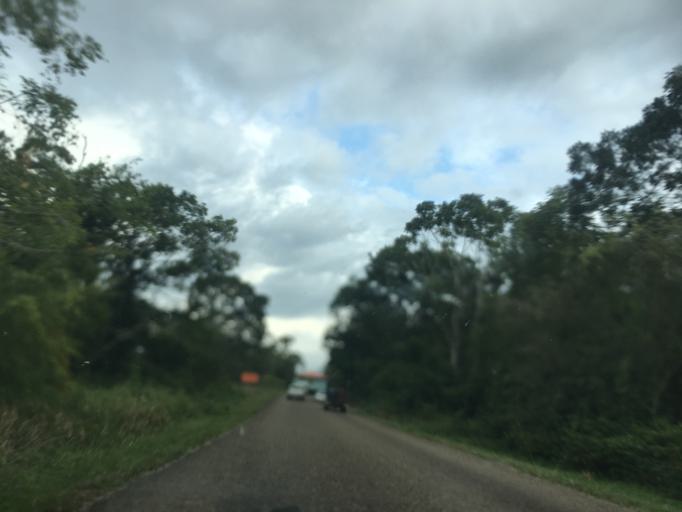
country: BZ
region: Cayo
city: San Ignacio
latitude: 17.2030
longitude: -88.9510
